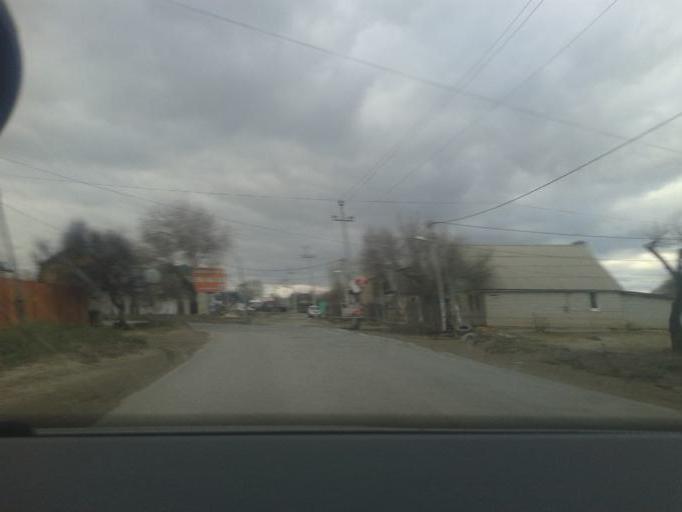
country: RU
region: Volgograd
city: Volgograd
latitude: 48.7019
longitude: 44.4692
